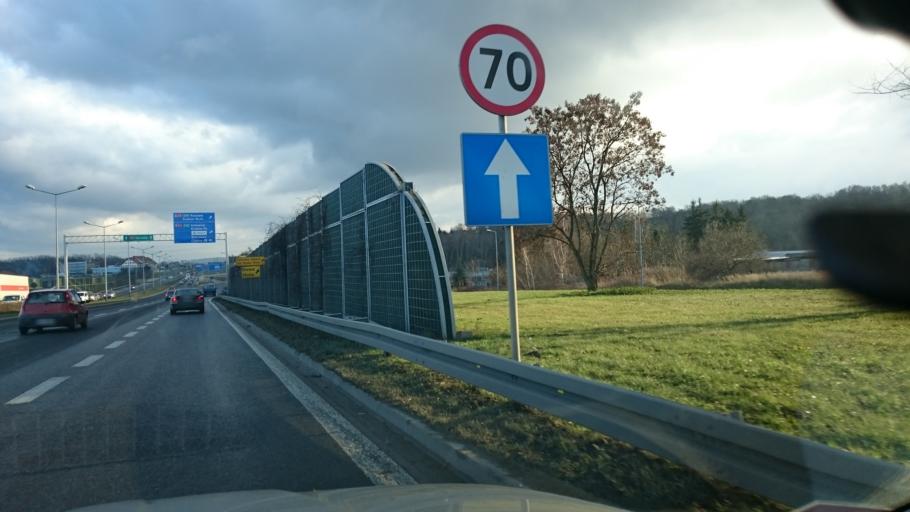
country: PL
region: Lesser Poland Voivodeship
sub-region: Powiat wielicki
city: Czarnochowice
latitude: 50.0075
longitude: 20.0143
